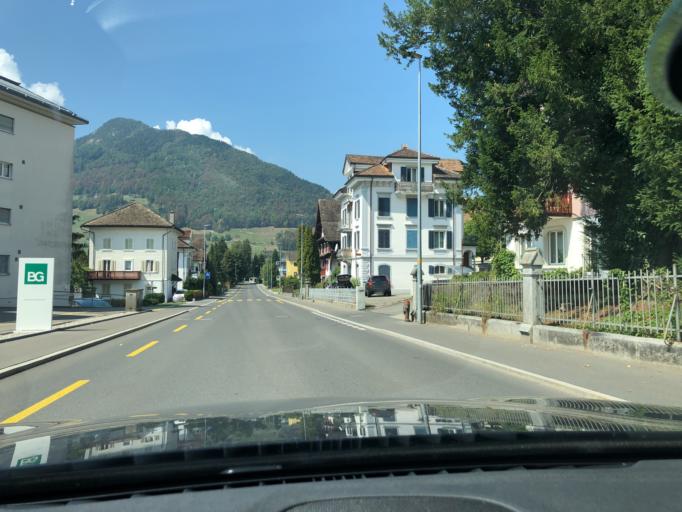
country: CH
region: Schwyz
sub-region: Bezirk Schwyz
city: Schwyz
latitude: 47.0228
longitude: 8.6433
